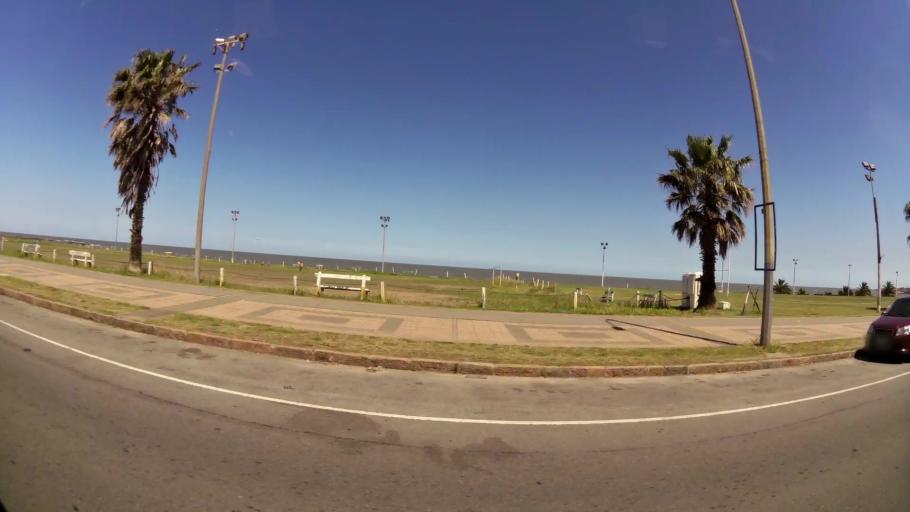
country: UY
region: Montevideo
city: Montevideo
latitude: -34.9257
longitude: -56.1560
